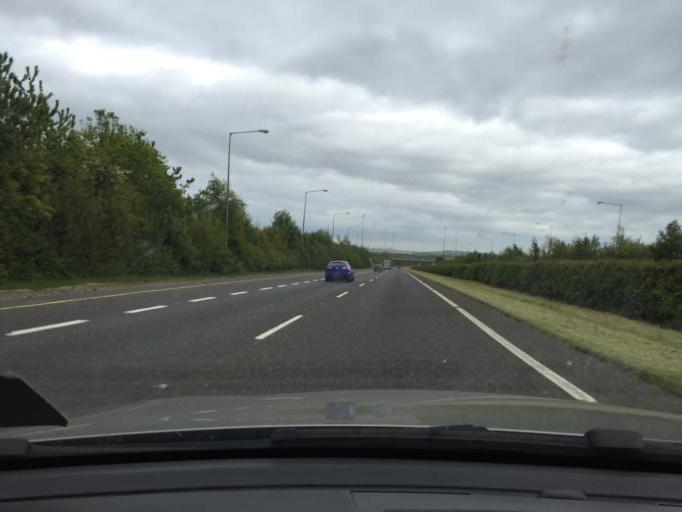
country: IE
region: Leinster
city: Balrothery
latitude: 53.6033
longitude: -6.2268
